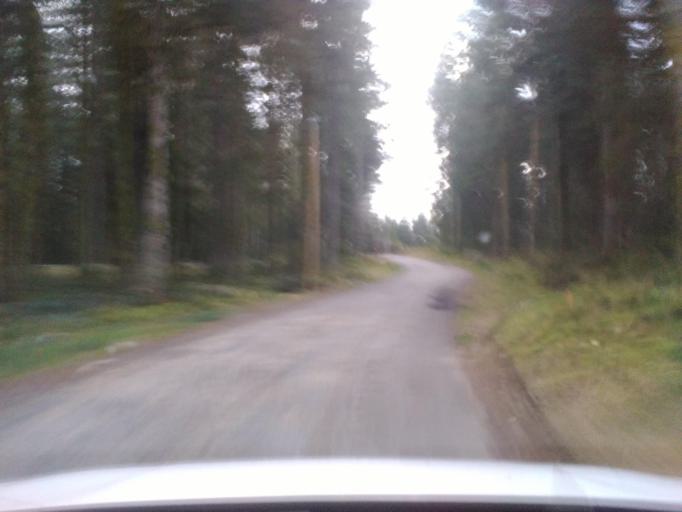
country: FR
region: Lorraine
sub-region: Departement des Vosges
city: Gerardmer
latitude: 48.0858
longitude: 6.8544
